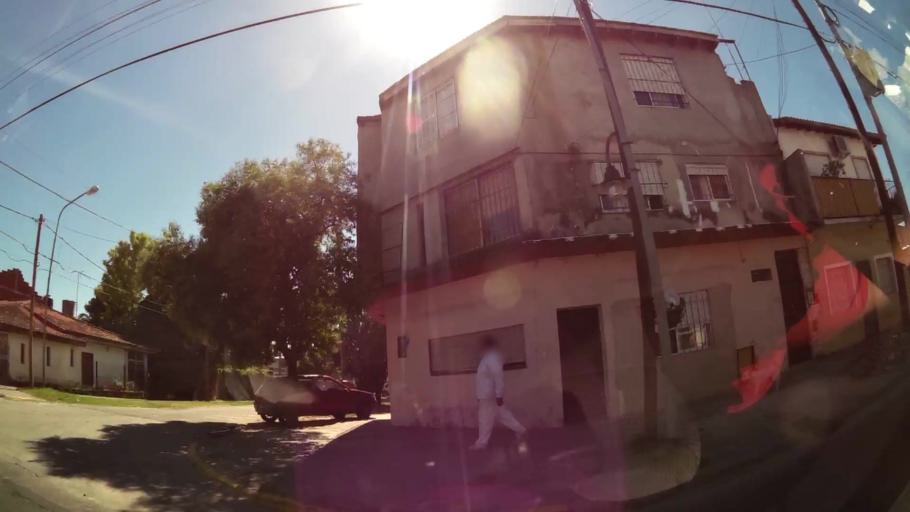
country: AR
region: Buenos Aires
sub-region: Partido de Tigre
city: Tigre
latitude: -34.4925
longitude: -58.6124
